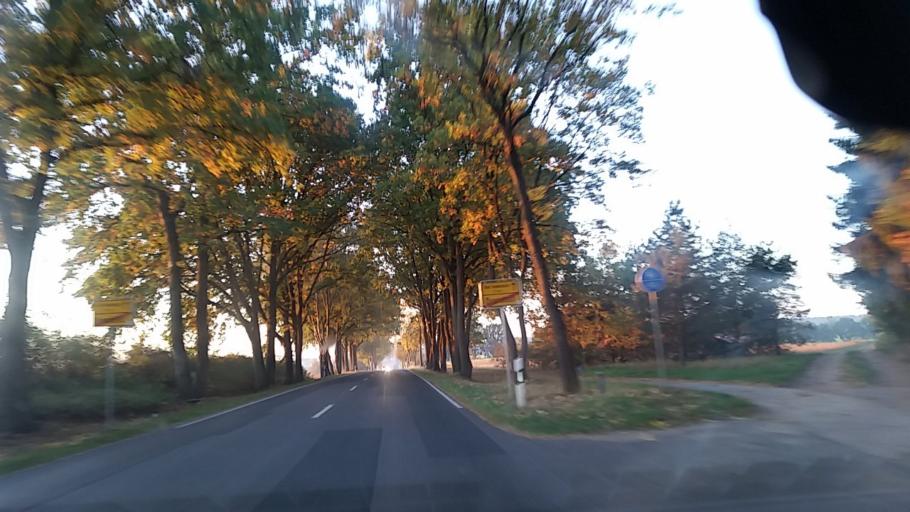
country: DE
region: Lower Saxony
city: Bodenteich
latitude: 52.8546
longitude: 10.6818
